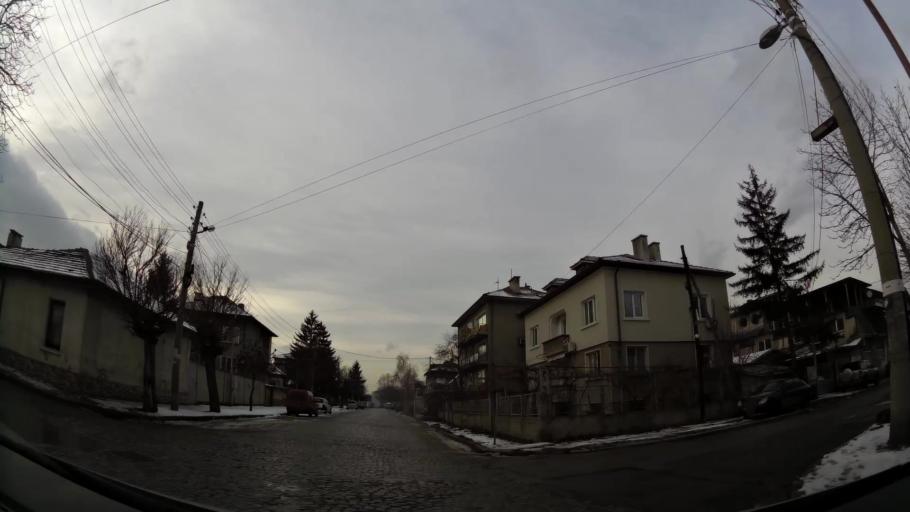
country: BG
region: Sofia-Capital
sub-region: Stolichna Obshtina
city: Sofia
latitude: 42.7215
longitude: 23.3385
